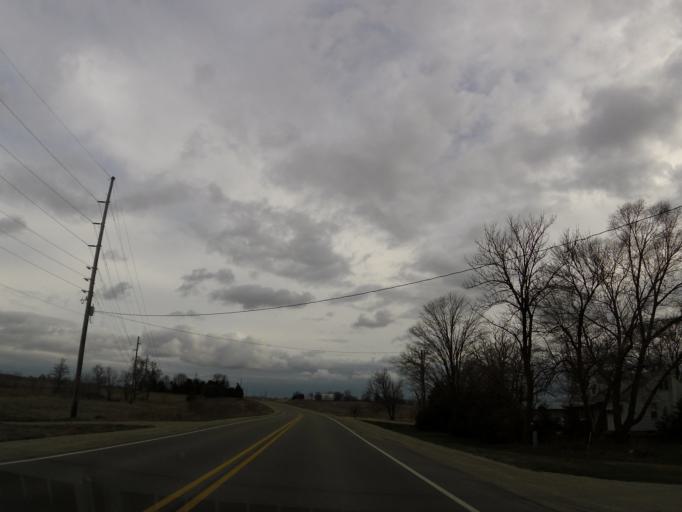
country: US
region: Iowa
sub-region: Black Hawk County
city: Elk Run Heights
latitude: 42.4917
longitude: -92.2195
